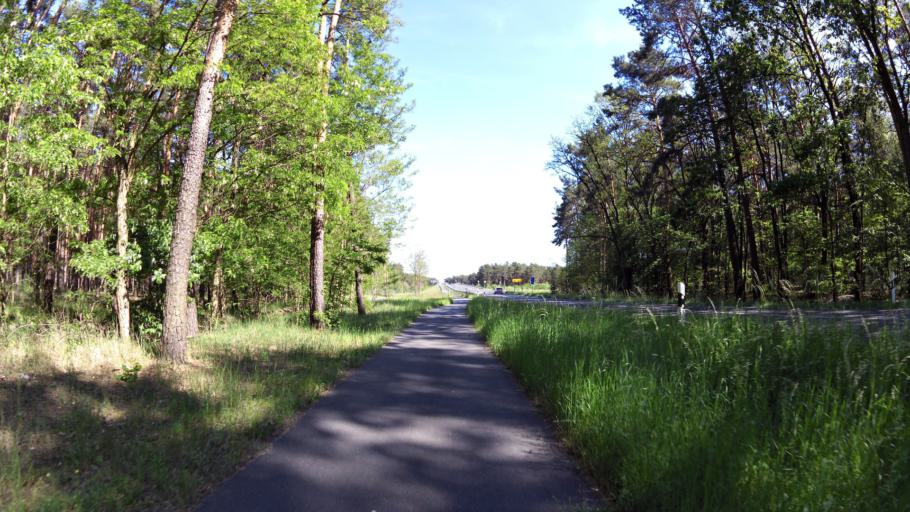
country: DE
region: Brandenburg
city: Mullrose
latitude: 52.2619
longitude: 14.4054
